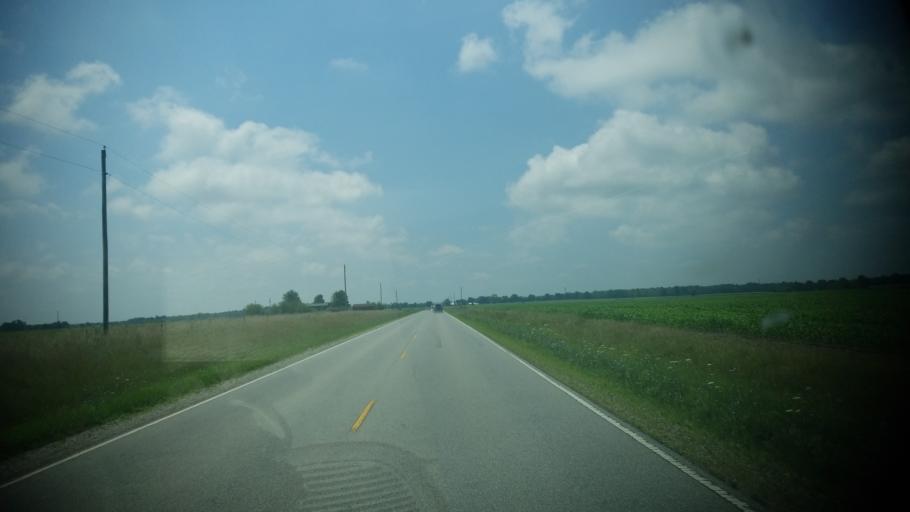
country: US
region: Illinois
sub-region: Wayne County
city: Fairfield
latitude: 38.4931
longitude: -88.3485
